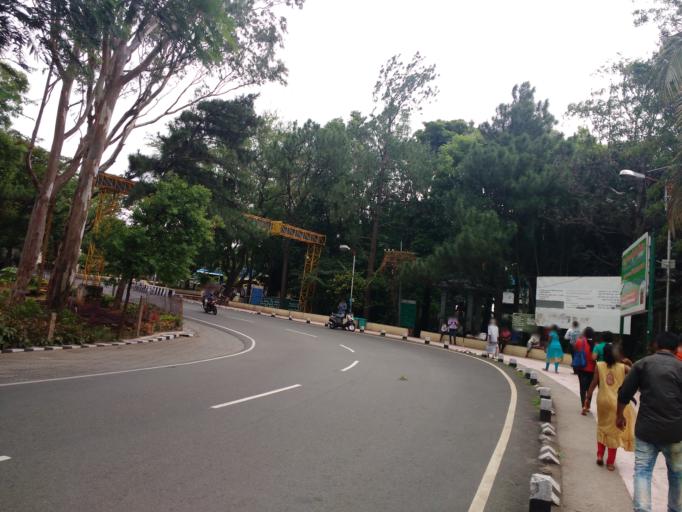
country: IN
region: Andhra Pradesh
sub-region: Chittoor
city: Tirumala
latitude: 13.6723
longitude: 79.3522
